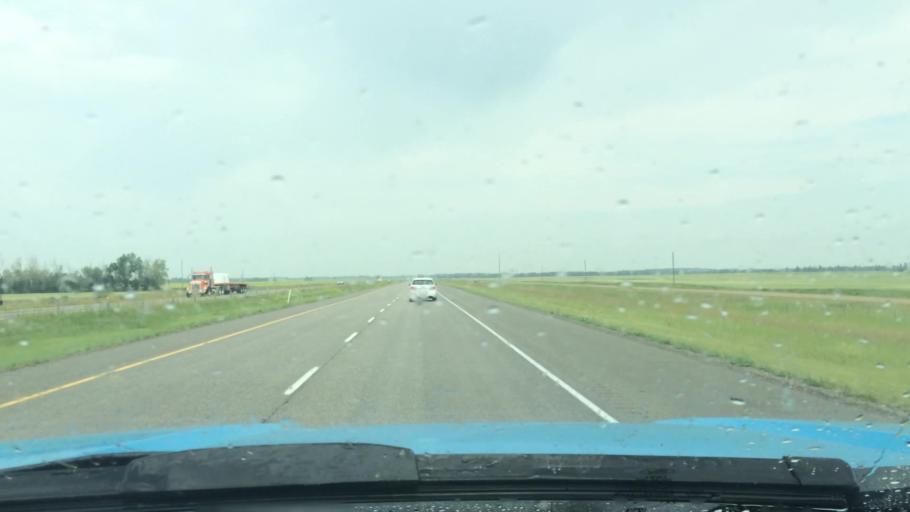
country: CA
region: Alberta
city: Olds
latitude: 51.7257
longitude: -114.0254
